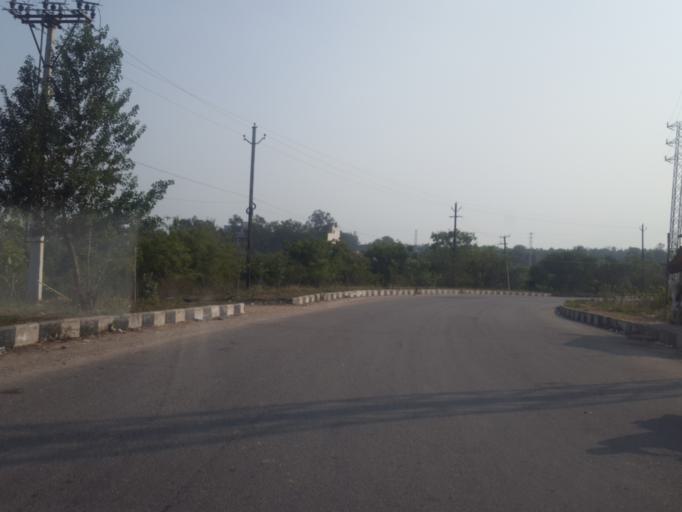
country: IN
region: Telangana
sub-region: Medak
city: Serilingampalle
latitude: 17.3988
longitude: 78.3122
